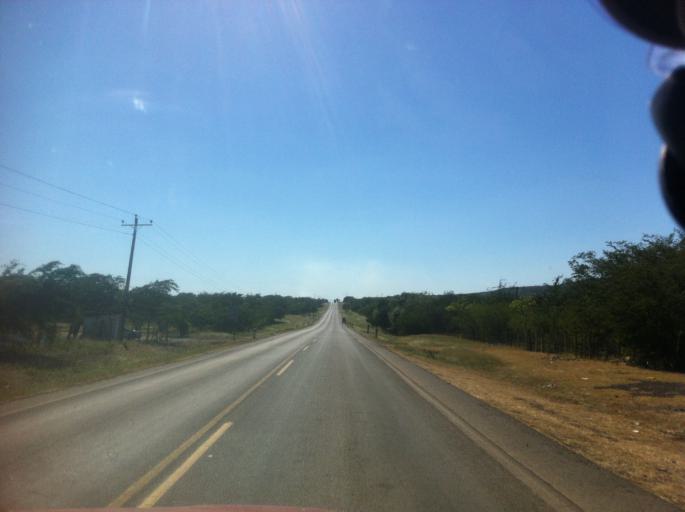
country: NI
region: Boaco
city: Teustepe
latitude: 12.3519
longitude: -85.9286
